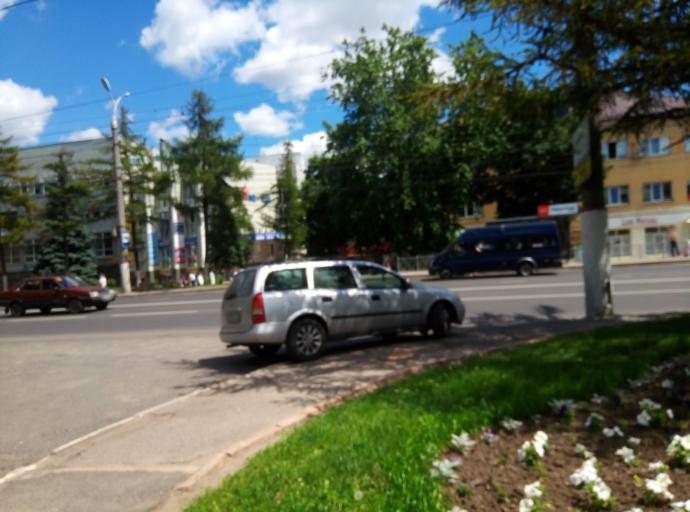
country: RU
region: Kursk
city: Kursk
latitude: 51.7551
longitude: 36.1889
